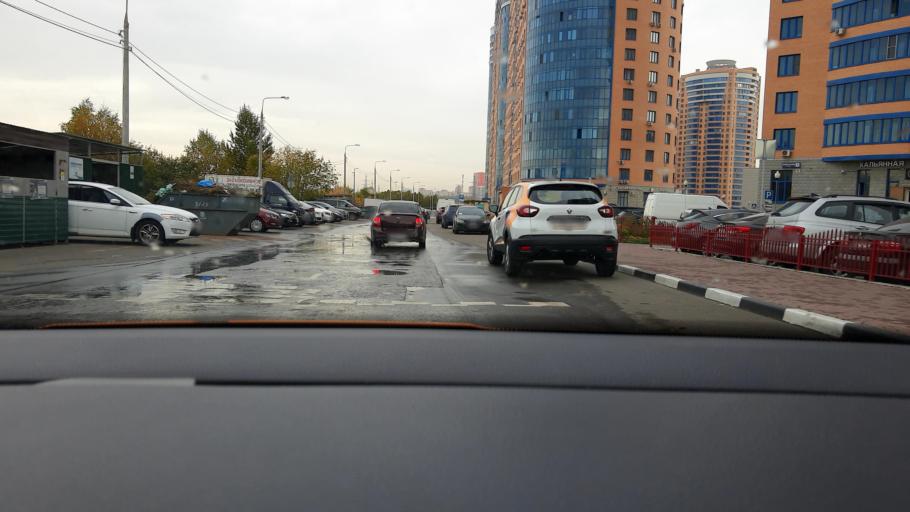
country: RU
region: Moscow
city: Ivanovskoye
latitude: 55.7712
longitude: 37.8461
